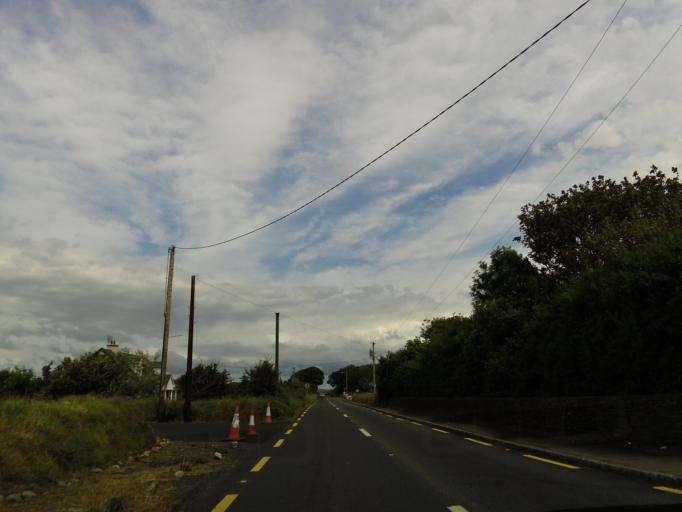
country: IE
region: Munster
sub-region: An Clar
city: Kilrush
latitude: 52.7327
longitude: -9.5149
